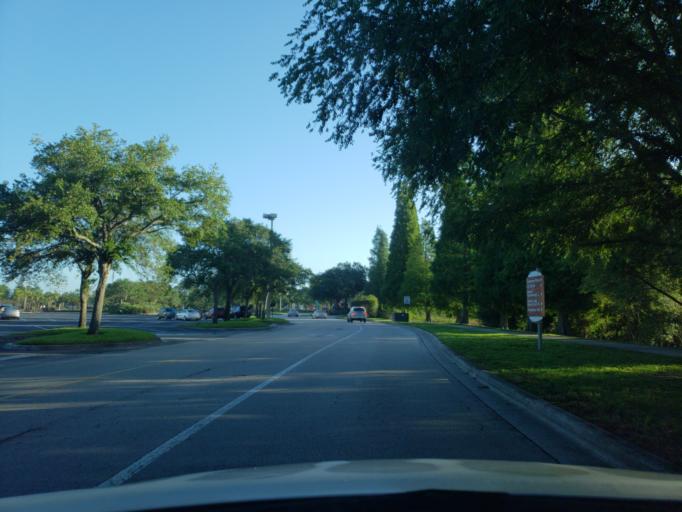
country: US
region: Florida
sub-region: Hillsborough County
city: Brandon
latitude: 27.9332
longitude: -82.3242
